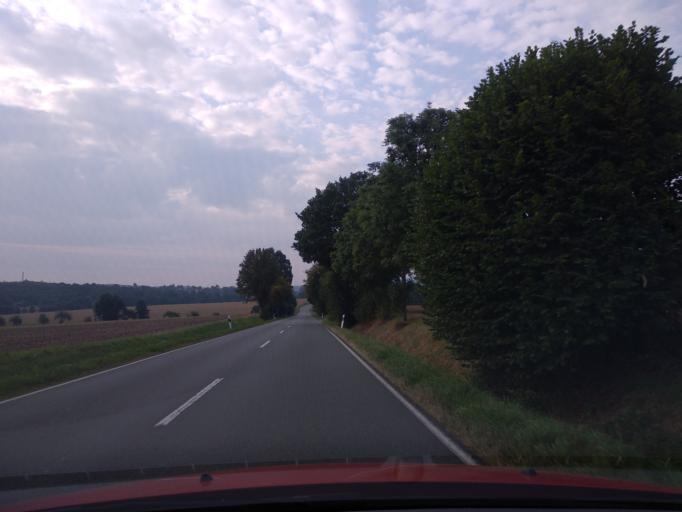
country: DE
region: Hesse
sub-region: Regierungsbezirk Kassel
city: Calden
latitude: 51.4139
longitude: 9.3477
